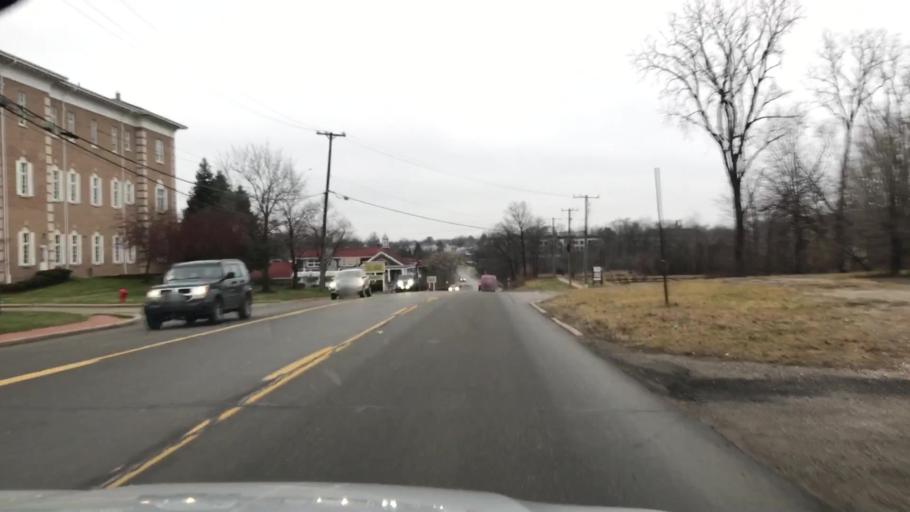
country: US
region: Michigan
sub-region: Wayne County
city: Plymouth
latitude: 42.3756
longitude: -83.4512
